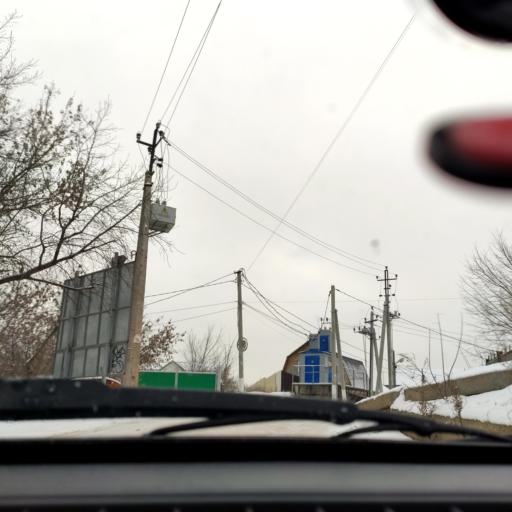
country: RU
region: Bashkortostan
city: Ufa
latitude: 54.7056
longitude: 55.9545
